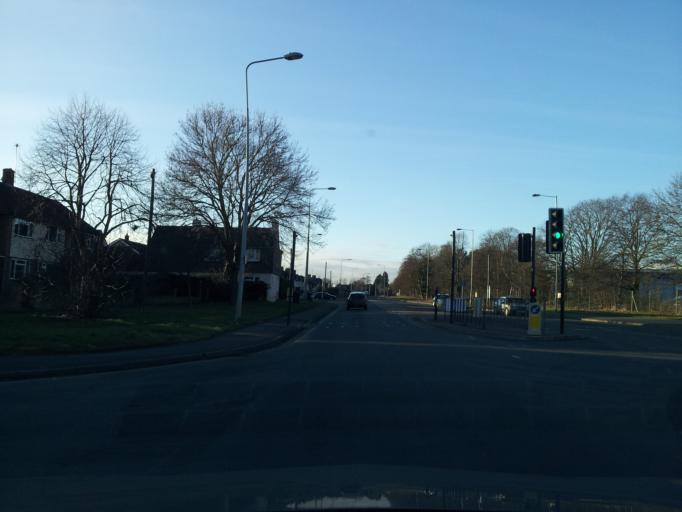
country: GB
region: England
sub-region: Northamptonshire
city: Northampton
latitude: 52.2566
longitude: -0.9441
